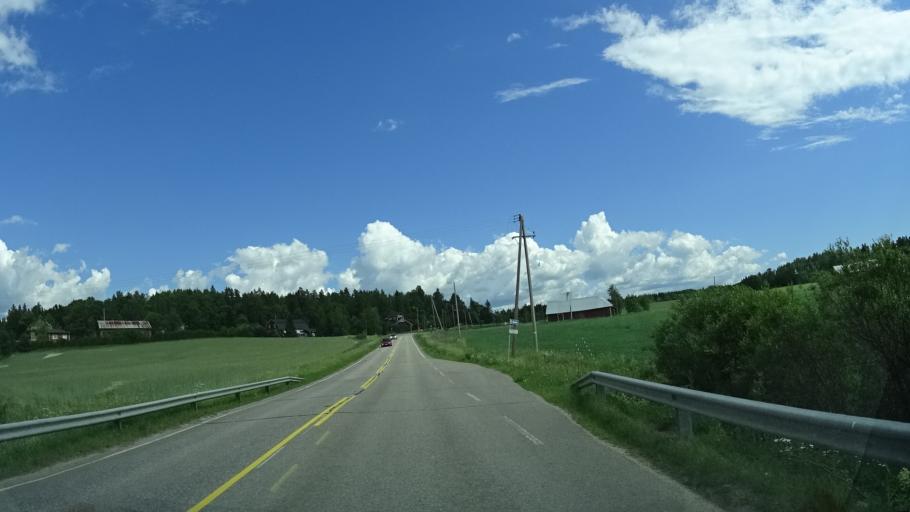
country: FI
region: Uusimaa
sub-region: Helsinki
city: Espoo
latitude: 60.3819
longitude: 24.6462
